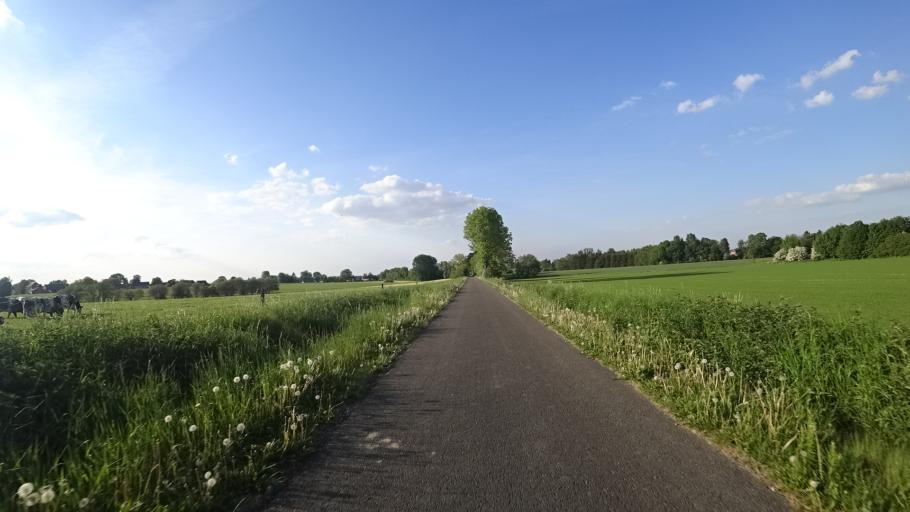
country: BE
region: Wallonia
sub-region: Province de Namur
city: Eghezee
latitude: 50.5393
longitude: 4.9018
